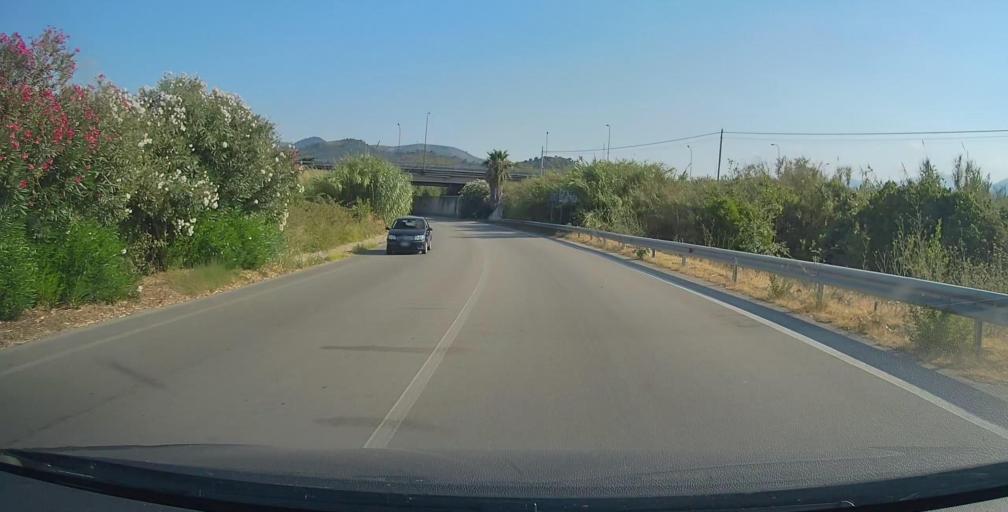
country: IT
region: Sicily
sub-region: Messina
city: Patti
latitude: 38.1440
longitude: 14.9959
